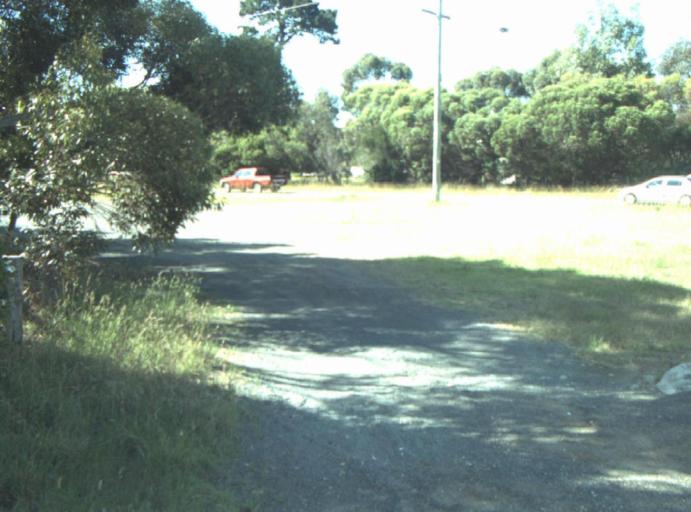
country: AU
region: Victoria
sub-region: Greater Geelong
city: Clifton Springs
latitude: -38.2416
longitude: 144.5731
